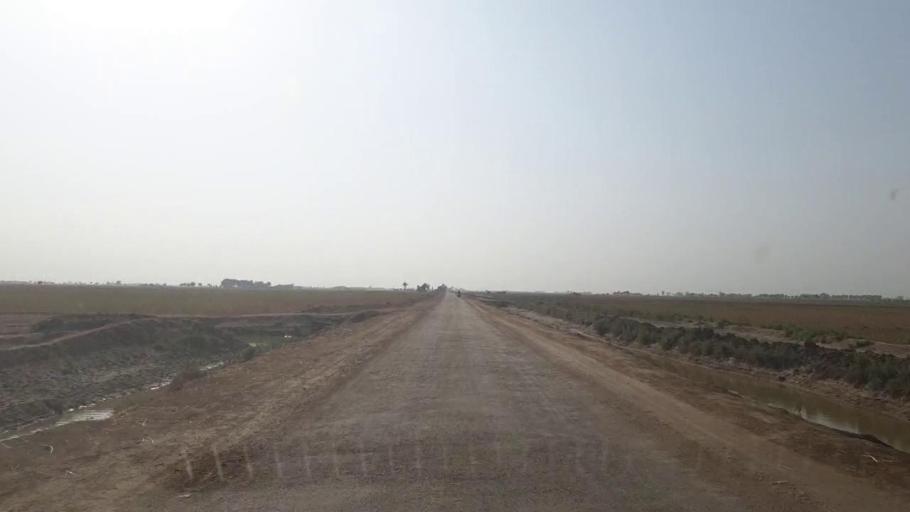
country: PK
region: Sindh
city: Kario
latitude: 24.5766
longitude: 68.5299
